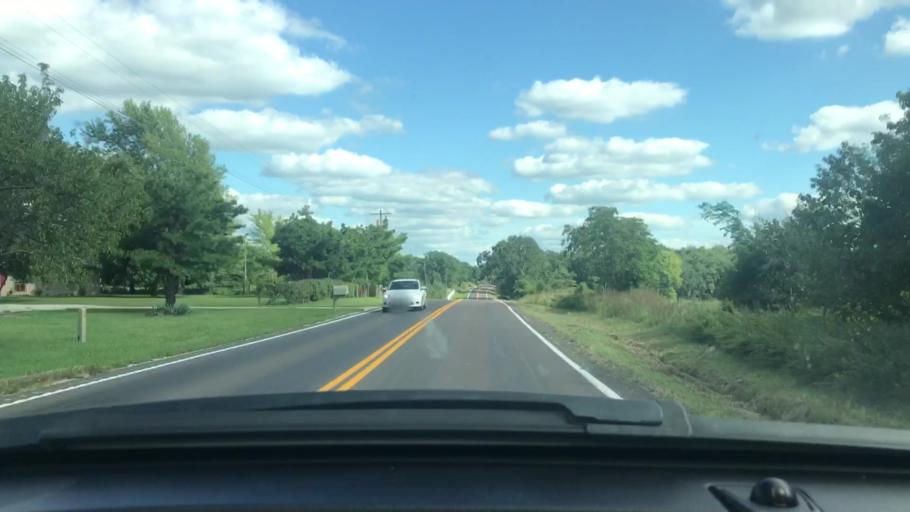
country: US
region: Missouri
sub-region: Wright County
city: Mountain Grove
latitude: 37.2330
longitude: -92.2984
